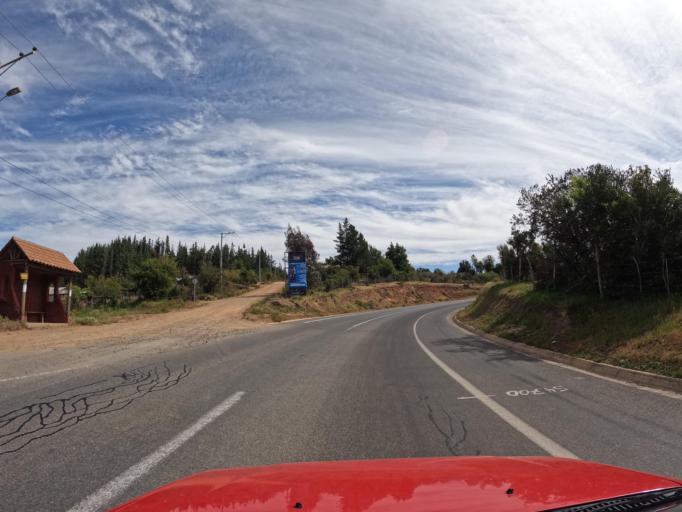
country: CL
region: Maule
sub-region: Provincia de Talca
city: Talca
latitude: -35.1710
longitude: -71.9736
